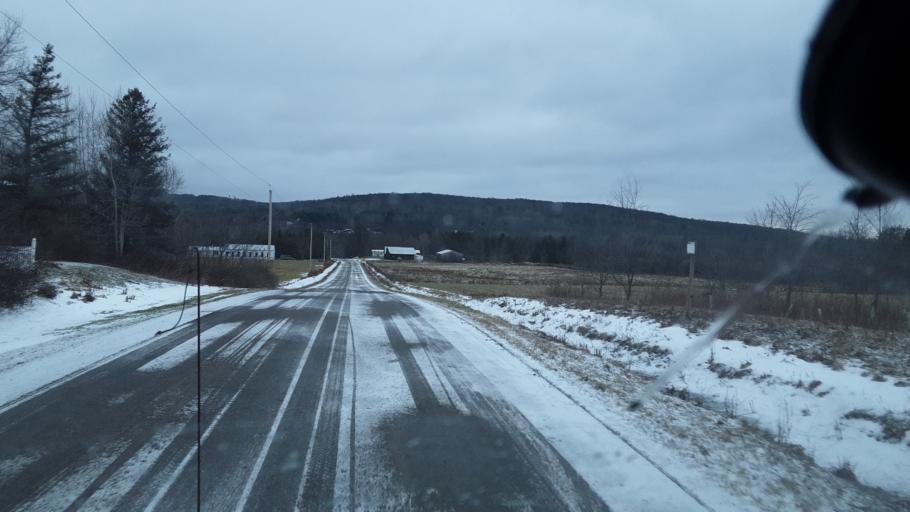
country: US
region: New York
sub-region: Allegany County
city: Friendship
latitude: 42.2974
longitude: -78.1625
